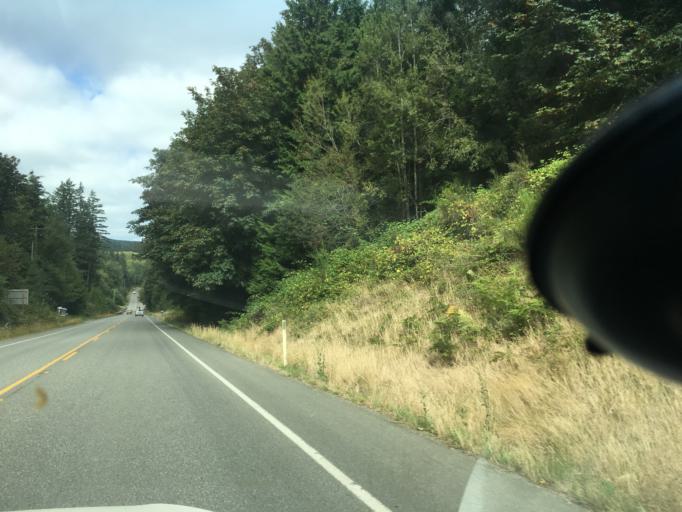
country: US
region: Washington
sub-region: Kitsap County
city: Kingston
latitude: 47.8090
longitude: -122.5764
